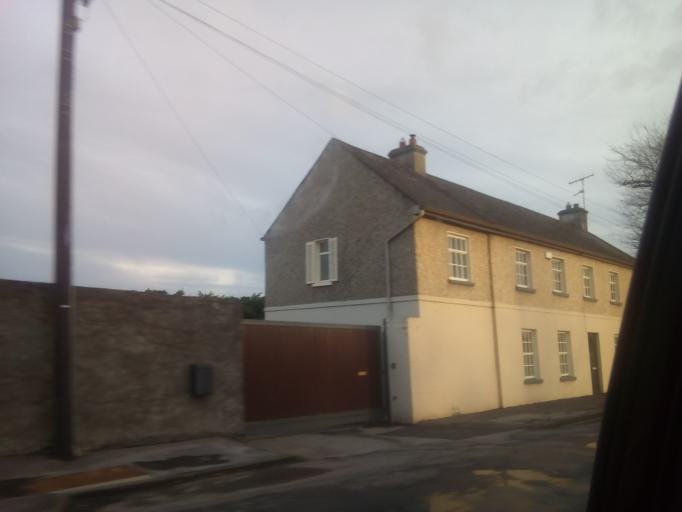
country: IE
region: Leinster
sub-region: Laois
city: Abbeyleix
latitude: 52.8433
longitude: -7.3988
